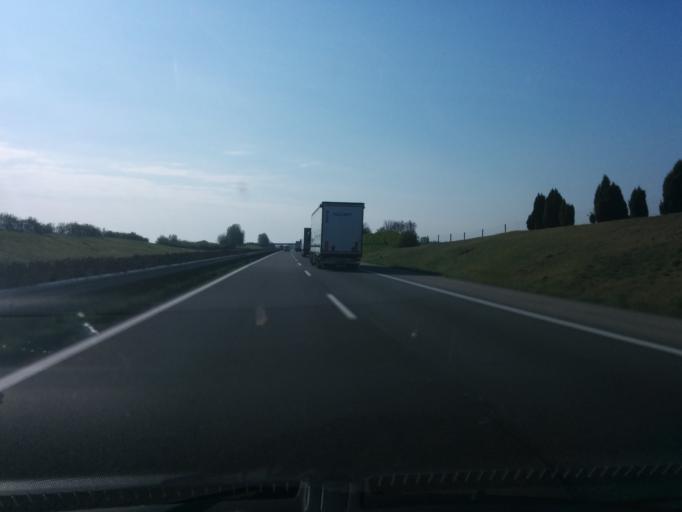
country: HU
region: Bacs-Kiskun
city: Varosfoeld
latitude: 46.8125
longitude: 19.7234
